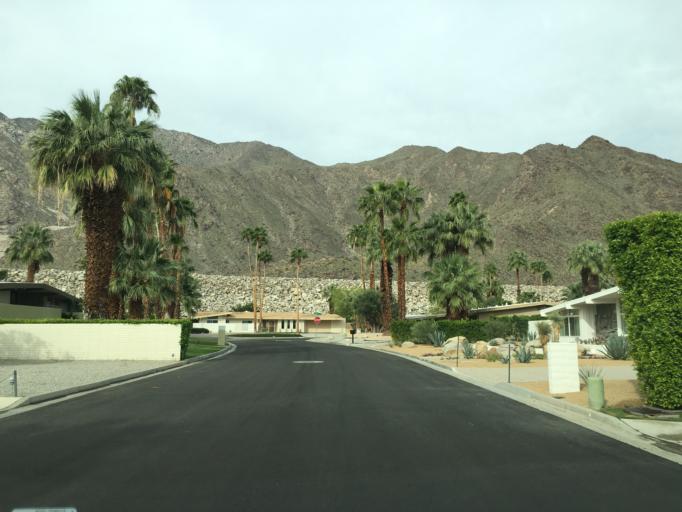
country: US
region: California
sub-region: Riverside County
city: Palm Springs
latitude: 33.8355
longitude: -116.5571
